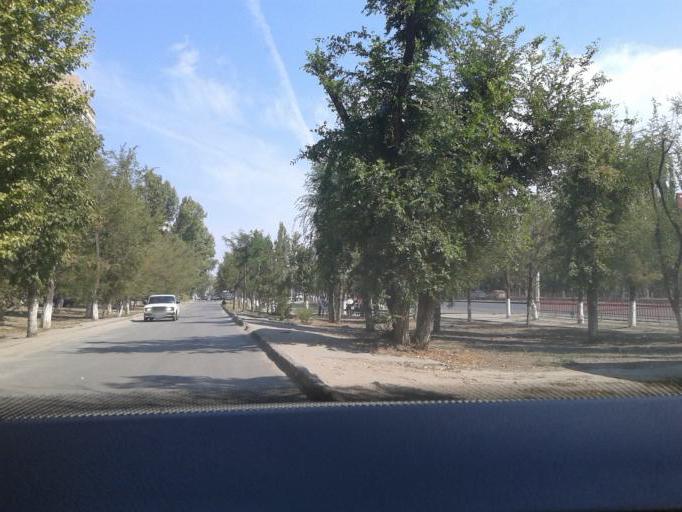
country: RU
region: Volgograd
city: Volgograd
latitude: 48.6188
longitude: 44.4234
